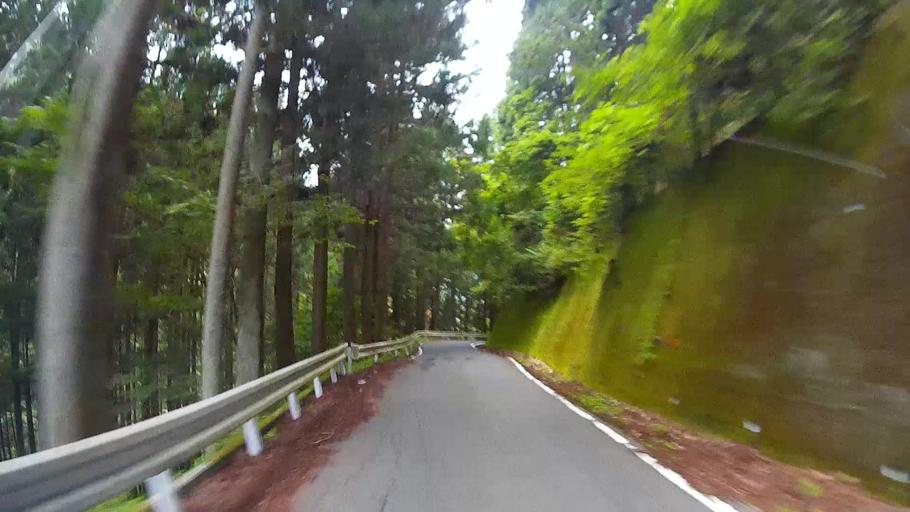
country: JP
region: Saitama
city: Chichibu
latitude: 35.9426
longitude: 138.8649
